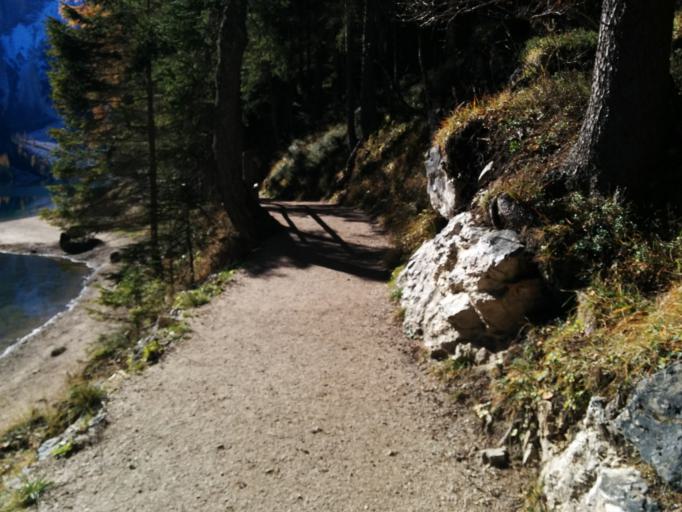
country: IT
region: Trentino-Alto Adige
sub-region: Bolzano
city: Braies
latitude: 46.6996
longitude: 12.0870
